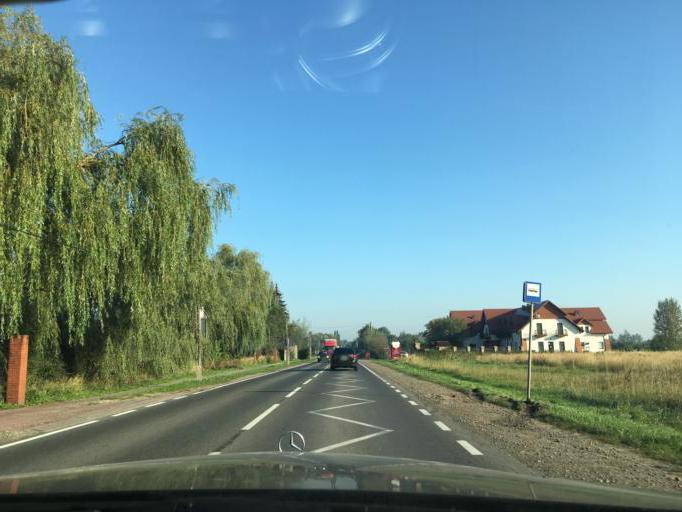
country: PL
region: Masovian Voivodeship
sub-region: Powiat grodziski
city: Grodzisk Mazowiecki
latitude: 52.1365
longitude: 20.6172
